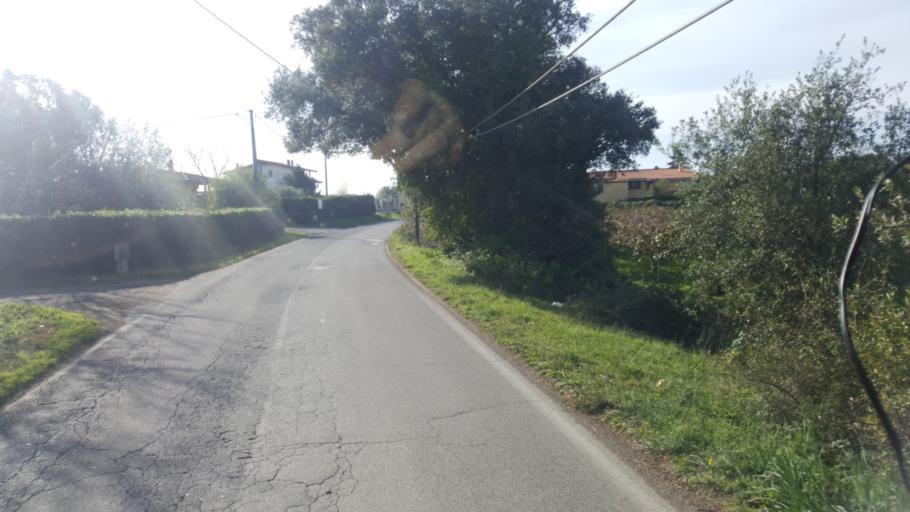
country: IT
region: Latium
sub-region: Provincia di Latina
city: Casalazzara
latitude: 41.6324
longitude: 12.6030
